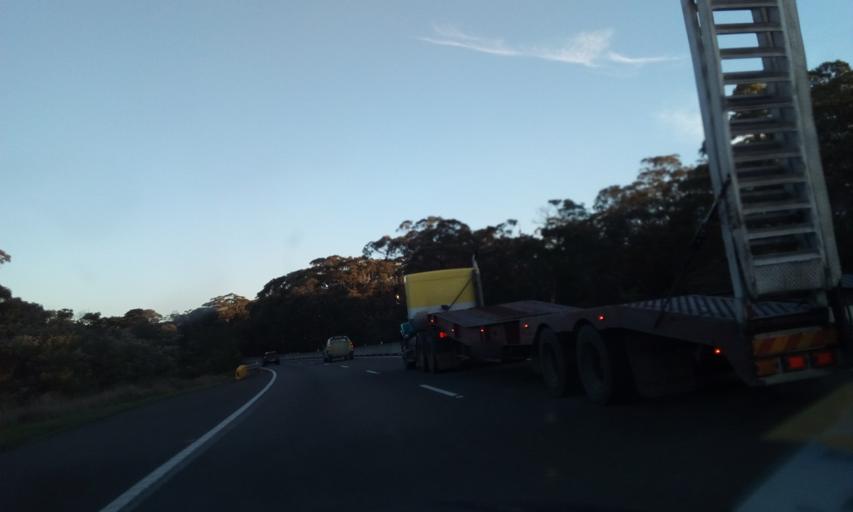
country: AU
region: New South Wales
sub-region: Wollongong
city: Mount Keira
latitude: -34.3467
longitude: 150.7979
